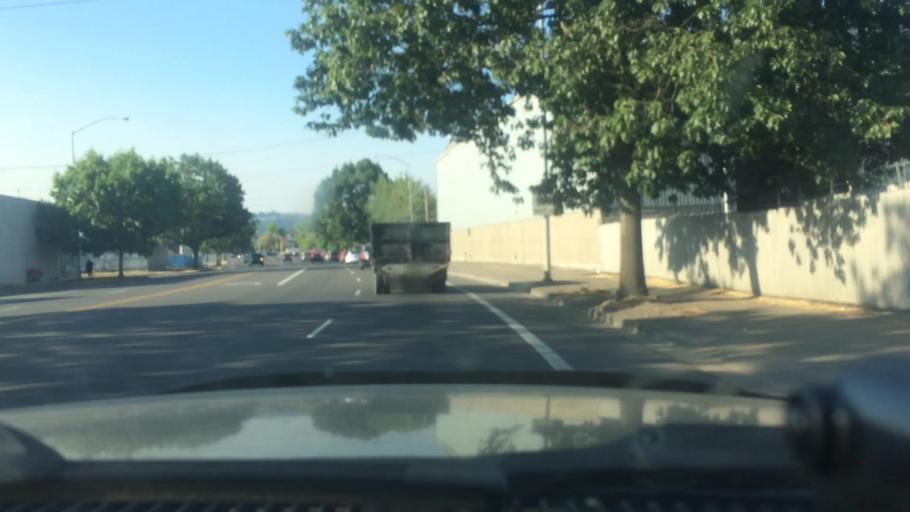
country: US
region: Oregon
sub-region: Lane County
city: Eugene
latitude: 44.0552
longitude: -123.1187
